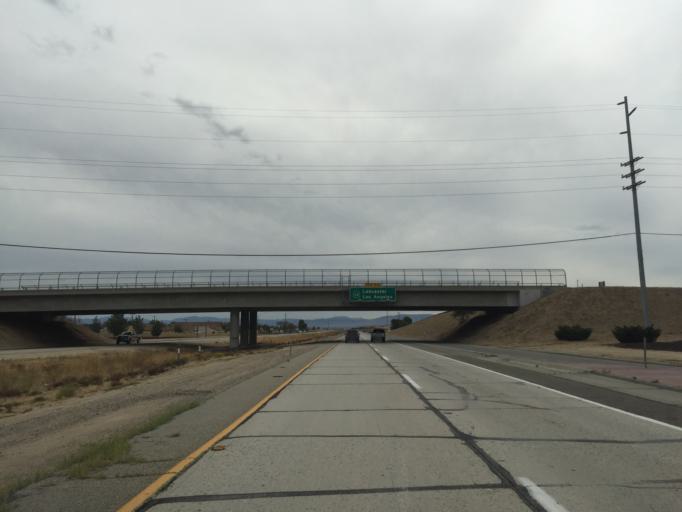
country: US
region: California
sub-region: Kern County
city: Rosamond
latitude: 34.8651
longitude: -118.1719
